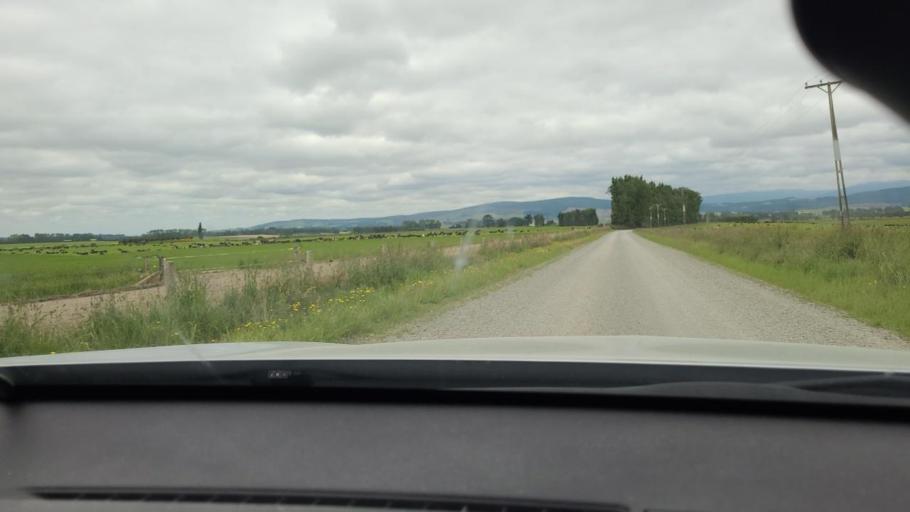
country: NZ
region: Southland
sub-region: Southland District
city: Riverton
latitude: -46.0806
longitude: 167.9781
